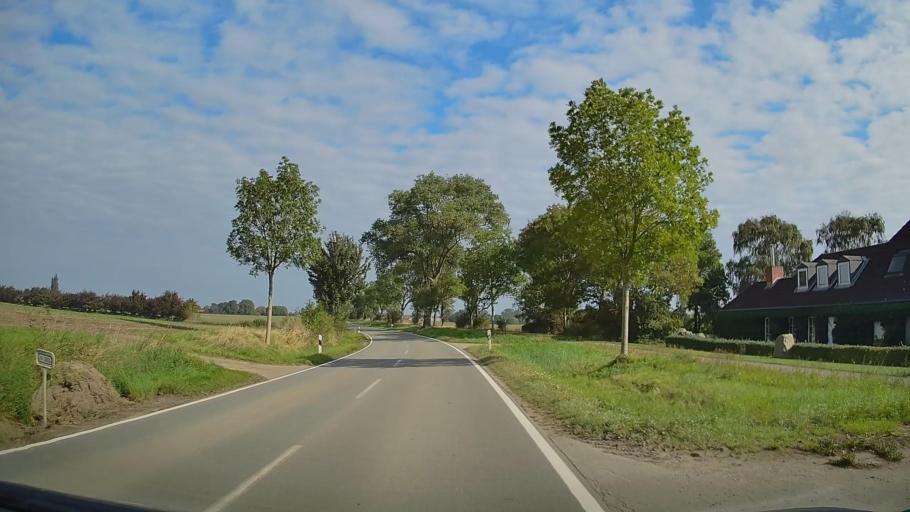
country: DE
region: Schleswig-Holstein
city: Gremersdorf
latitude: 54.3461
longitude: 10.9053
